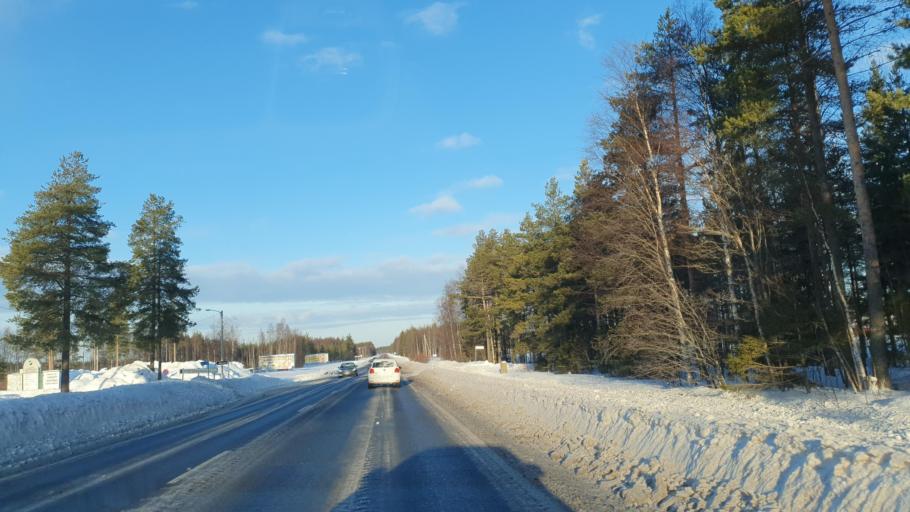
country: FI
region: Northern Ostrobothnia
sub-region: Oulunkaari
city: Utajaervi
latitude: 64.7402
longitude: 26.4571
